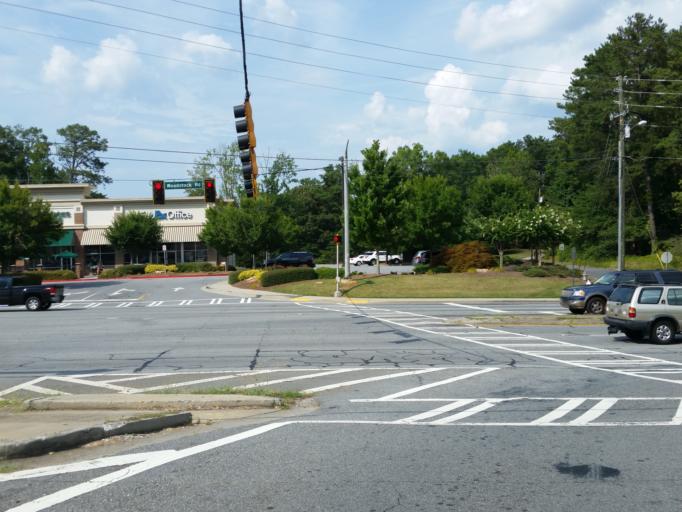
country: US
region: Georgia
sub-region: Fulton County
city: Roswell
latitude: 34.0619
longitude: -84.4207
